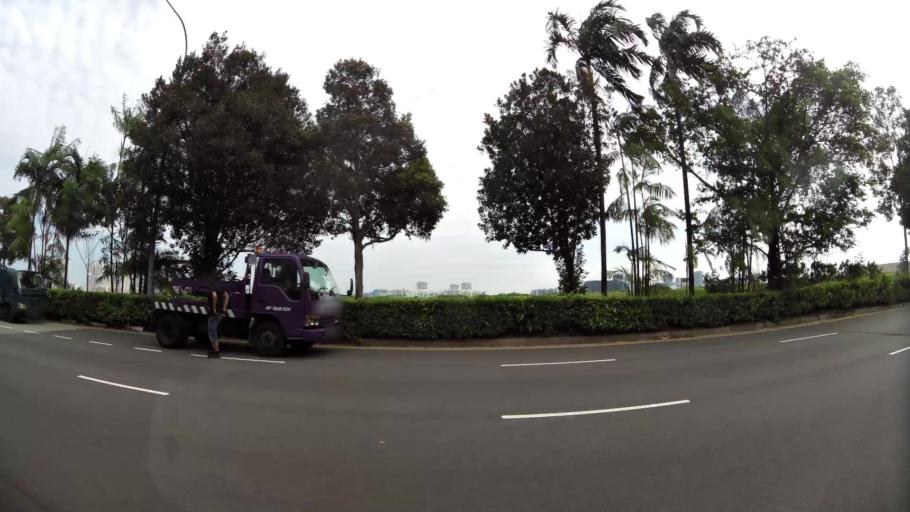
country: SG
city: Singapore
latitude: 1.3094
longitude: 103.7387
